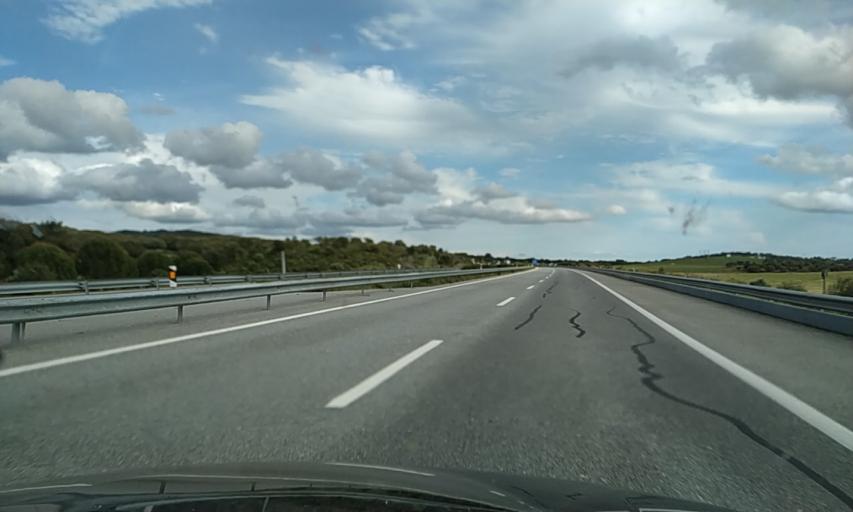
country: PT
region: Evora
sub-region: Estremoz
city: Estremoz
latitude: 38.8152
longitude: -7.5584
